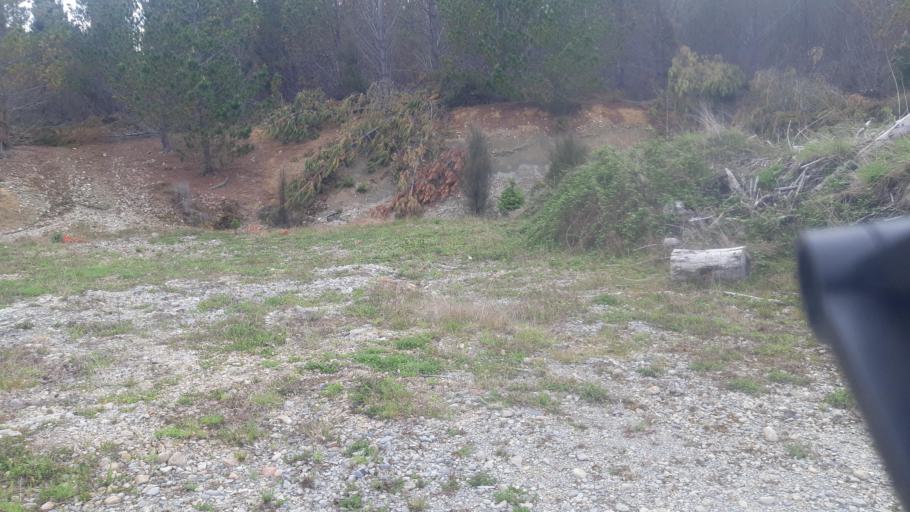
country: NZ
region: Tasman
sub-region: Tasman District
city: Wakefield
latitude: -41.7690
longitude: 172.8016
